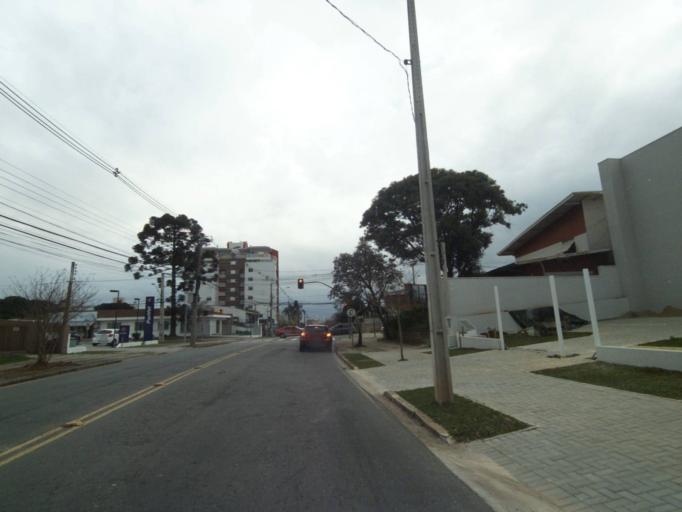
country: BR
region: Parana
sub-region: Curitiba
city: Curitiba
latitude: -25.4012
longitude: -49.2628
